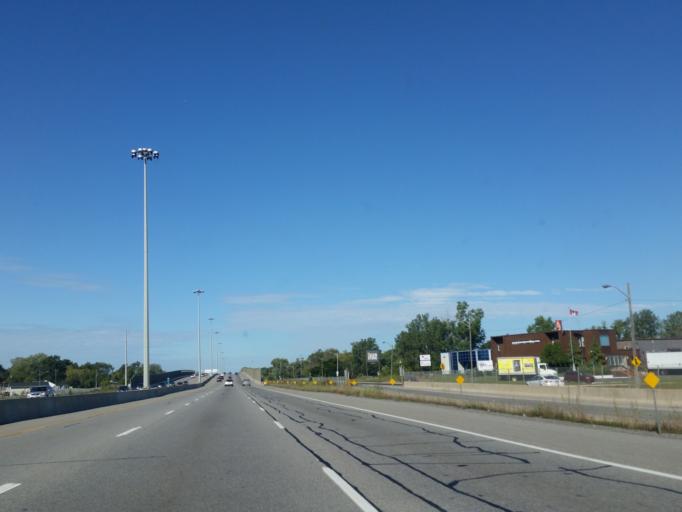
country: CA
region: Ontario
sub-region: Regional Municipality of Niagara
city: St. Catharines
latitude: 43.1698
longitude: -79.2165
